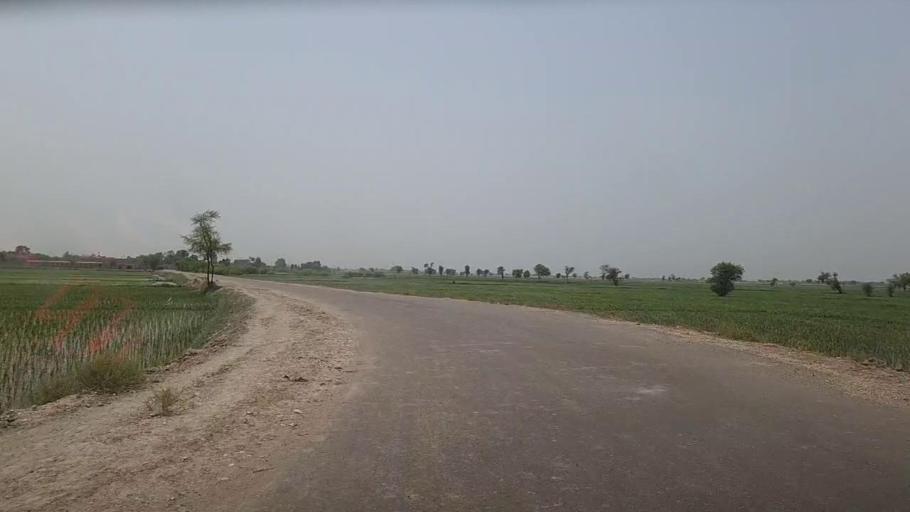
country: PK
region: Sindh
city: Sita Road
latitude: 27.0642
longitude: 67.9035
